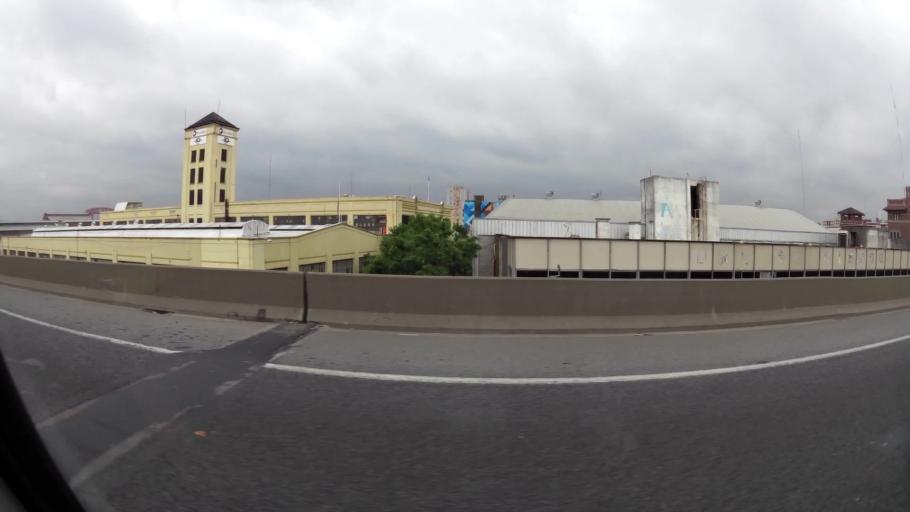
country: AR
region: Buenos Aires F.D.
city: Buenos Aires
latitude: -34.6296
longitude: -58.3552
